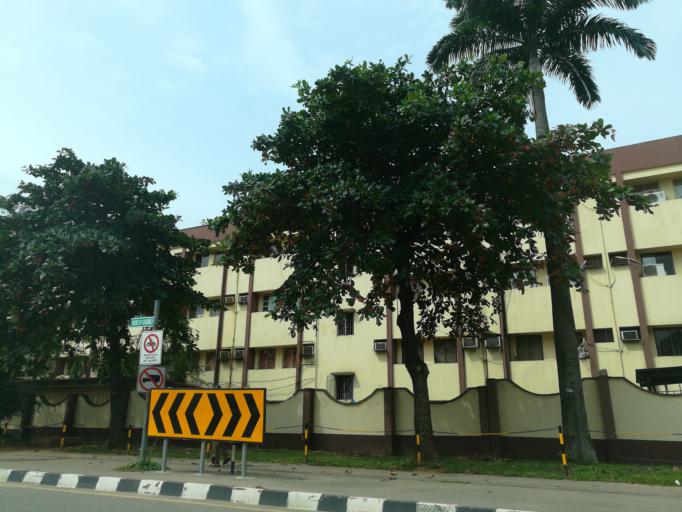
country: NG
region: Lagos
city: Ikeja
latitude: 6.6158
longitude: 3.3630
